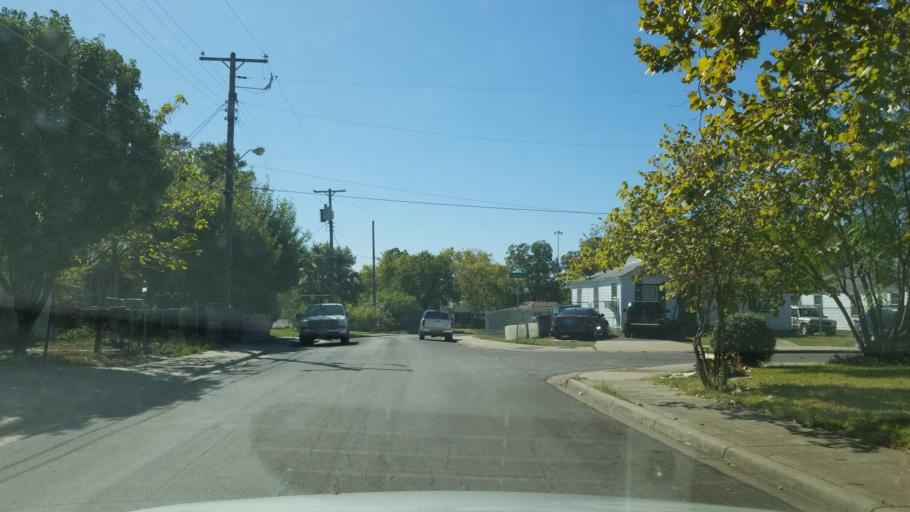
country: US
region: Texas
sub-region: Dallas County
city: Dallas
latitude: 32.7813
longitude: -96.7453
